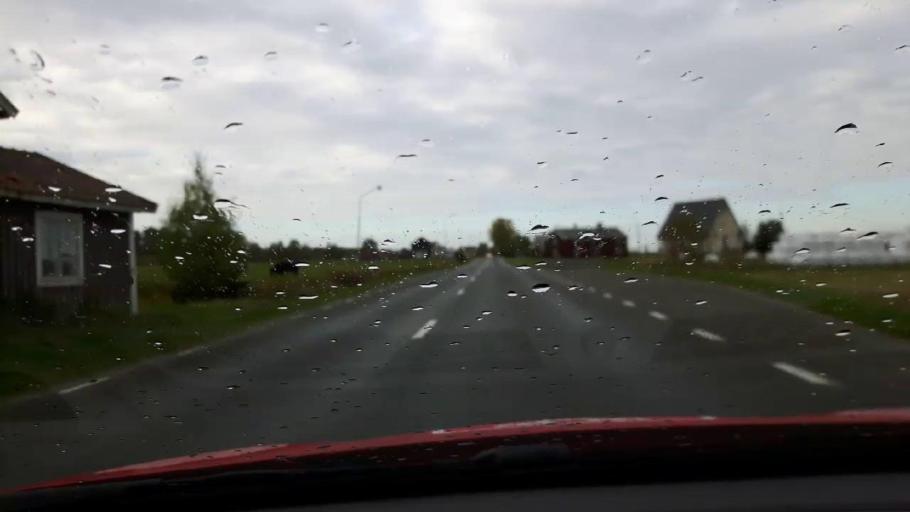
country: SE
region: Jaemtland
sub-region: Krokoms Kommun
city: Krokom
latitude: 63.1287
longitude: 14.2882
